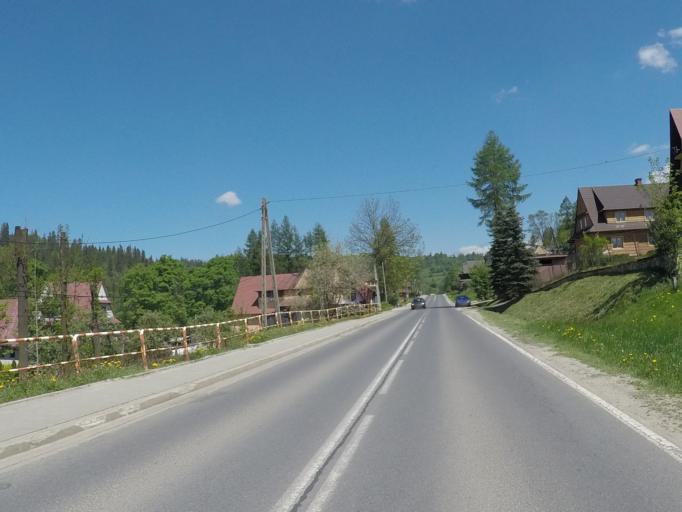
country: PL
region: Lesser Poland Voivodeship
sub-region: Powiat tatrzanski
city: Poronin
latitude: 49.3339
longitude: 20.0491
